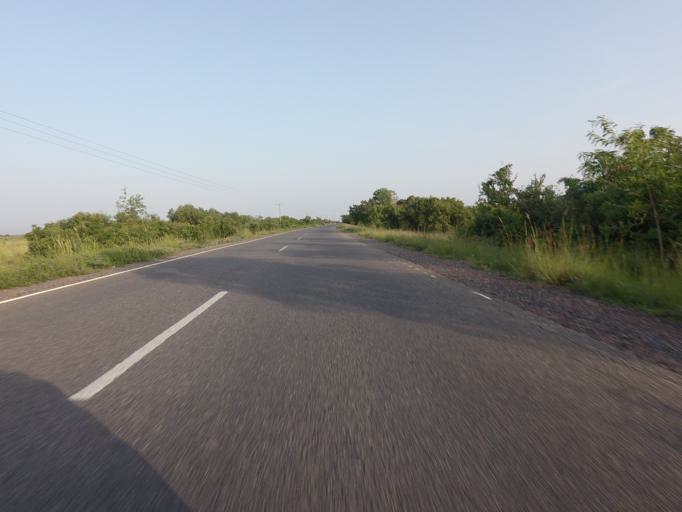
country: GH
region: Volta
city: Anloga
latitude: 5.9129
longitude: 0.7086
